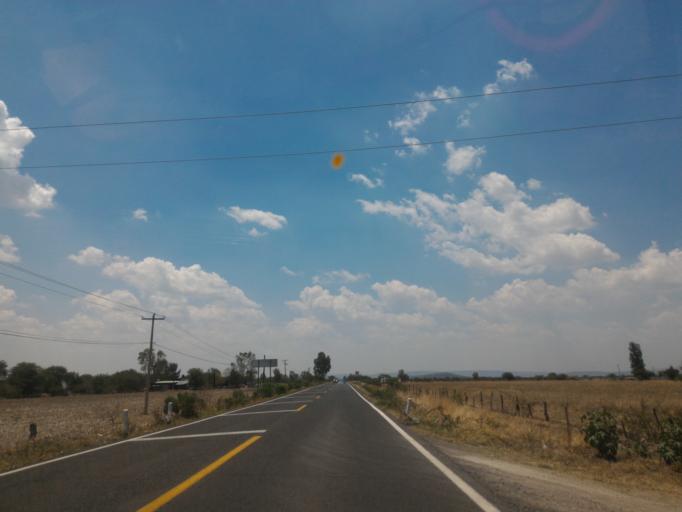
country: MX
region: Guanajuato
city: Ciudad Manuel Doblado
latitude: 20.7581
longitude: -101.9662
